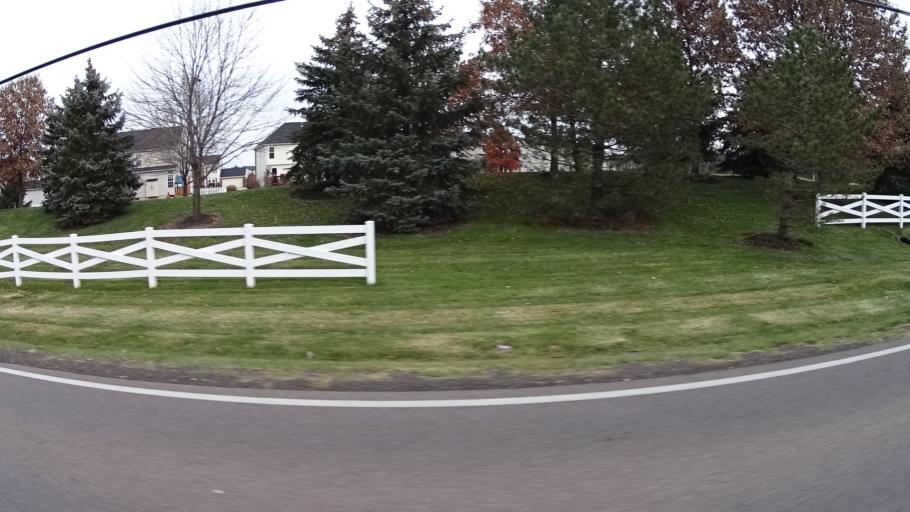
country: US
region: Ohio
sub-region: Lorain County
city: Sheffield
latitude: 41.4089
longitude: -82.0629
